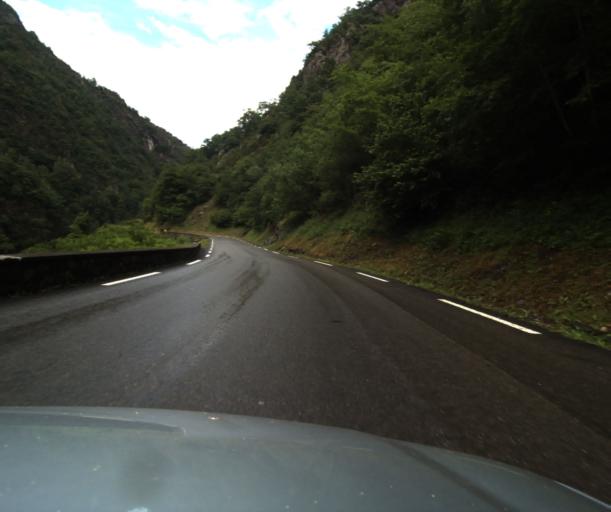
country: FR
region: Midi-Pyrenees
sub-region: Departement des Hautes-Pyrenees
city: Luz-Saint-Sauveur
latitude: 42.8491
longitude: -0.0065
